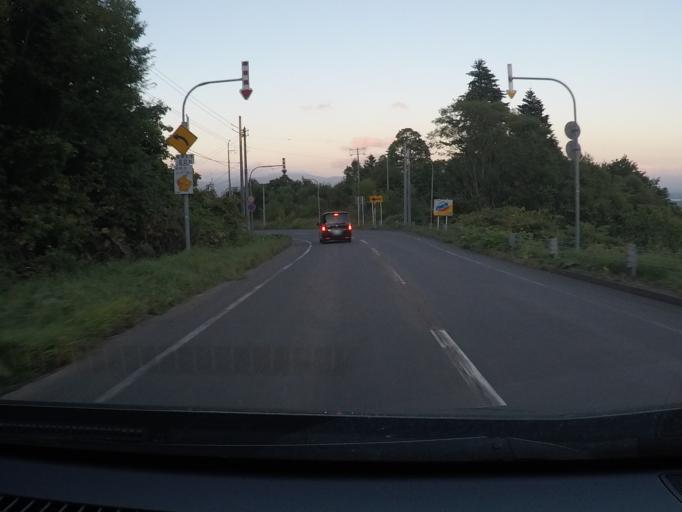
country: JP
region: Hokkaido
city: Nayoro
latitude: 44.3790
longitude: 142.3322
